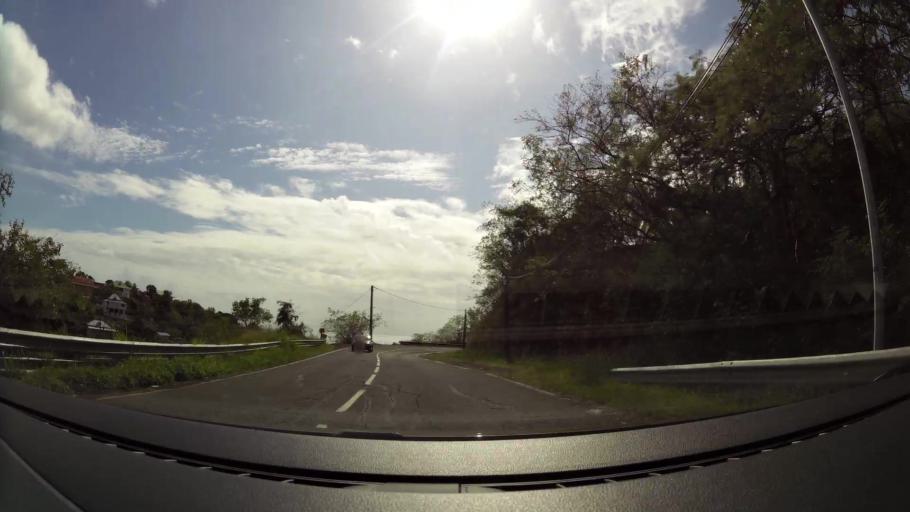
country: GP
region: Guadeloupe
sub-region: Guadeloupe
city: Vieux-Habitants
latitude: 16.0439
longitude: -61.7537
